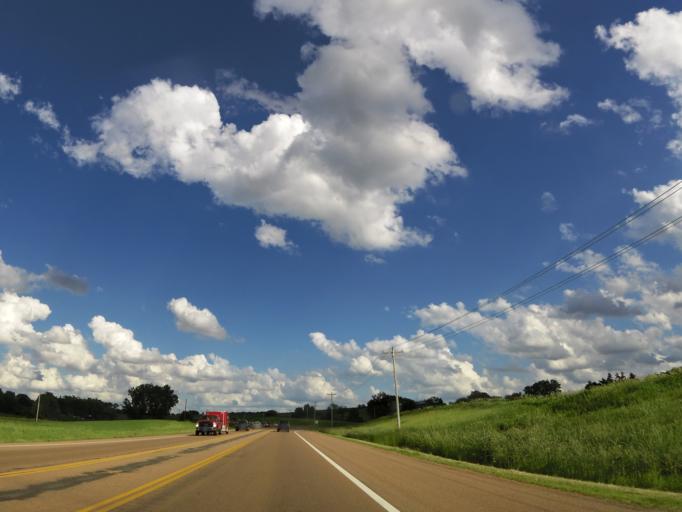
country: US
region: Minnesota
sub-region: Carver County
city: Waconia
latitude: 44.8320
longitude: -93.7623
